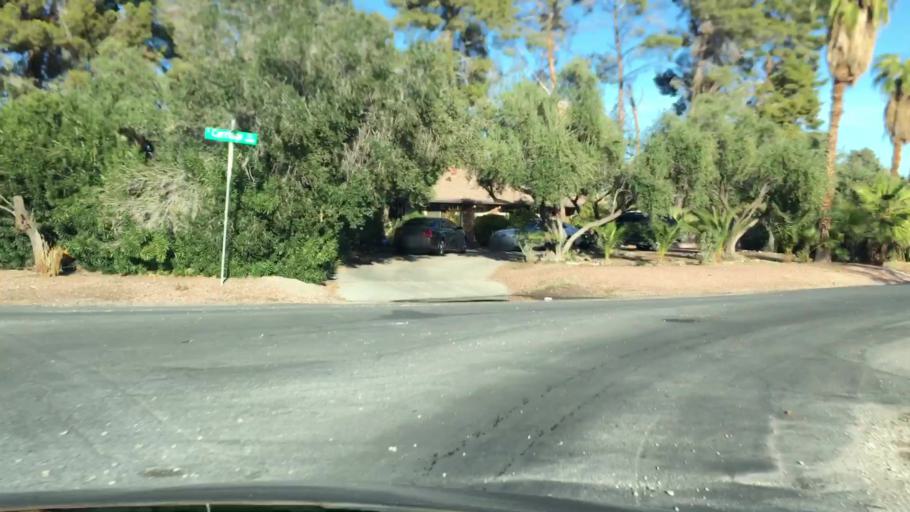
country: US
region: Nevada
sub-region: Clark County
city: Paradise
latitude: 36.1057
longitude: -115.1275
